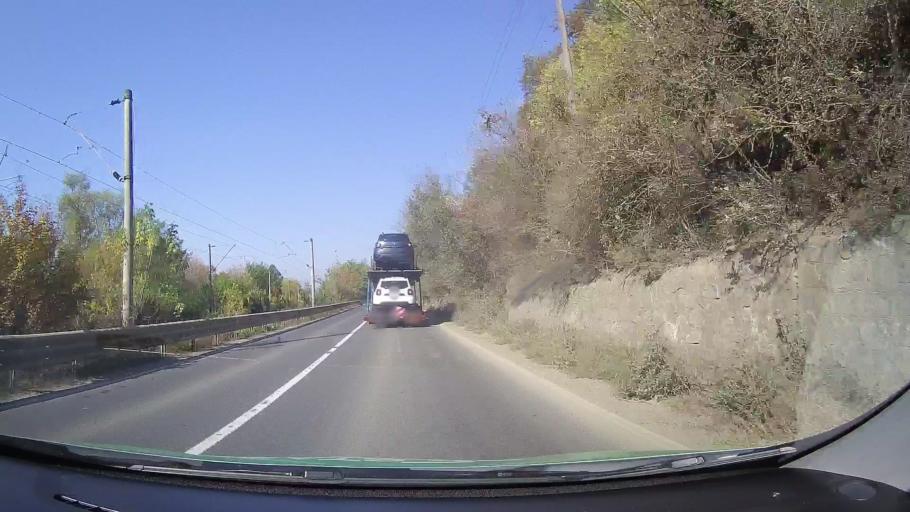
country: RO
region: Arad
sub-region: Comuna Bata
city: Bata
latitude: 46.0689
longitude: 22.0410
